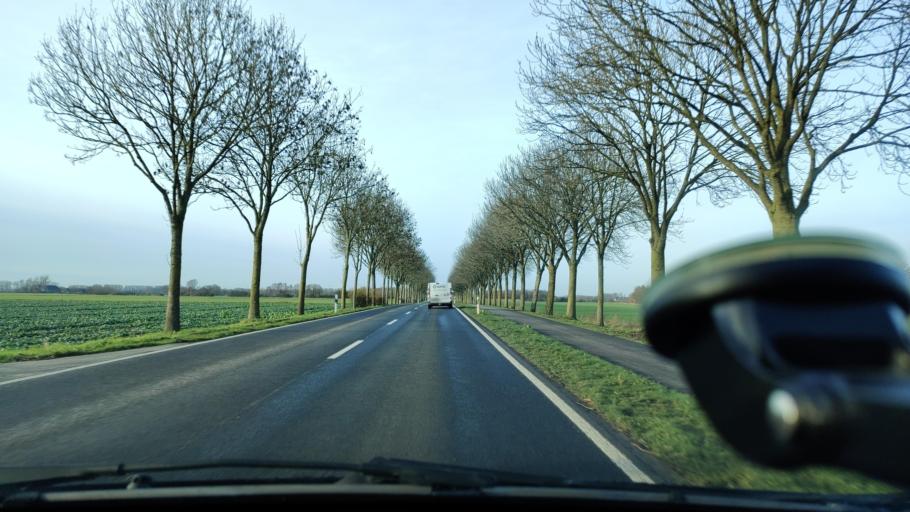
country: DE
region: North Rhine-Westphalia
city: Kalkar
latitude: 51.7469
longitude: 6.3223
